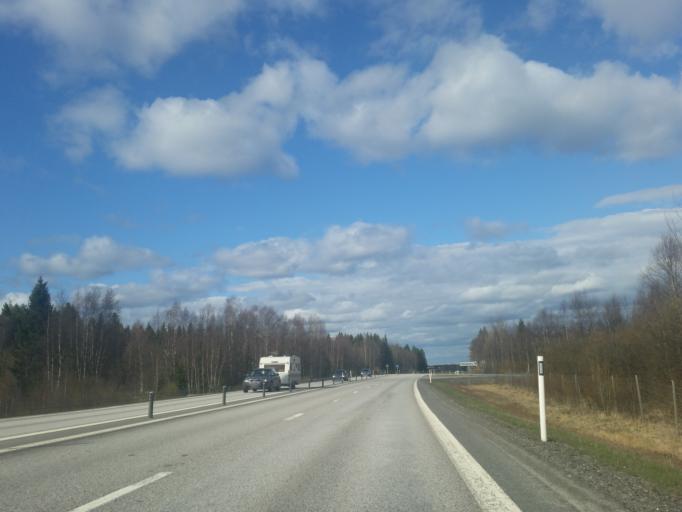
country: SE
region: Vaesterbotten
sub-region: Robertsfors Kommun
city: Robertsfors
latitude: 64.0660
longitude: 20.8502
